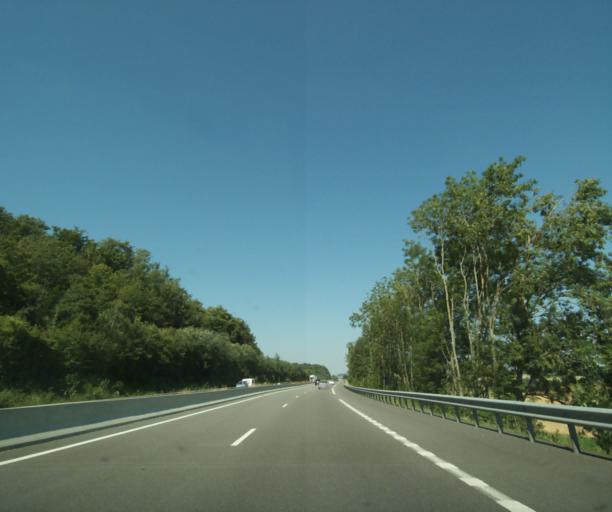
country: FR
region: Lorraine
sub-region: Departement de la Meuse
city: Lerouville
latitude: 48.7047
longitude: 5.5093
